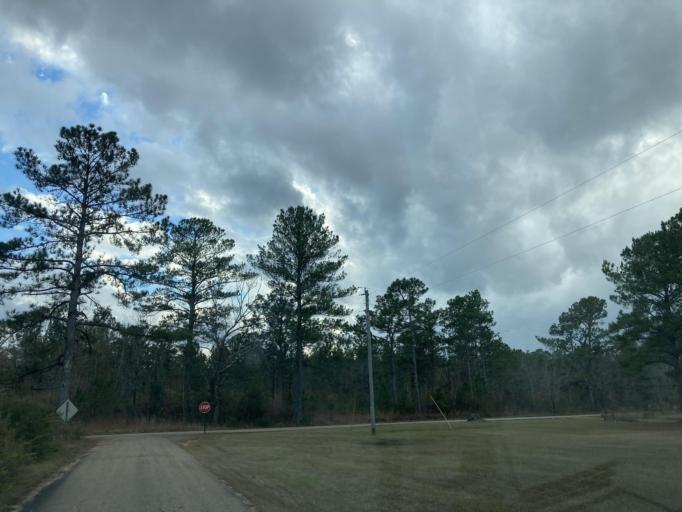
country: US
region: Mississippi
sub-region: Lamar County
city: Purvis
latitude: 31.1625
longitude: -89.6008
